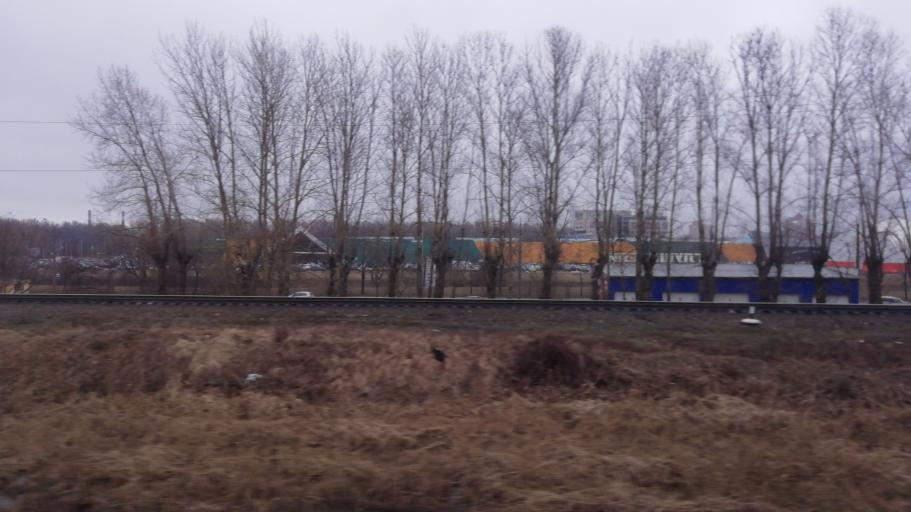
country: RU
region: St.-Petersburg
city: Kupchino
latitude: 59.8765
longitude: 30.3524
